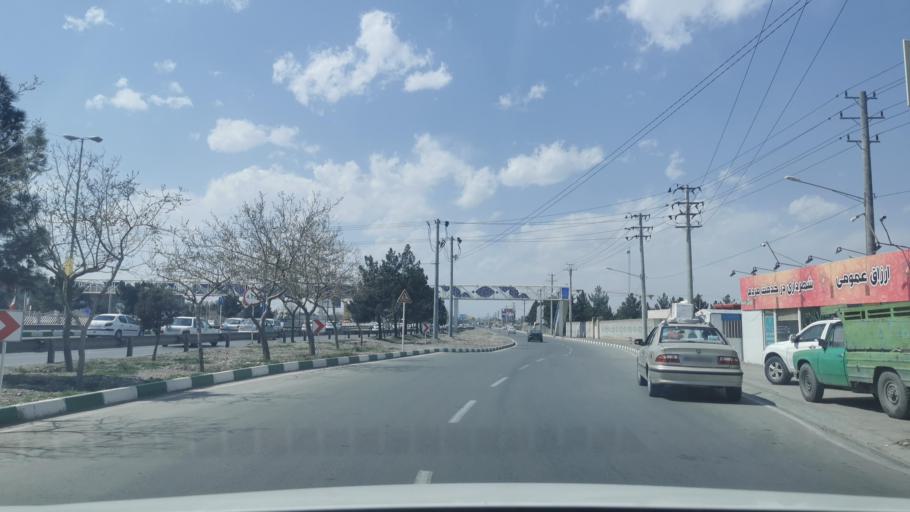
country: IR
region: Razavi Khorasan
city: Mashhad
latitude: 36.3950
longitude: 59.4984
